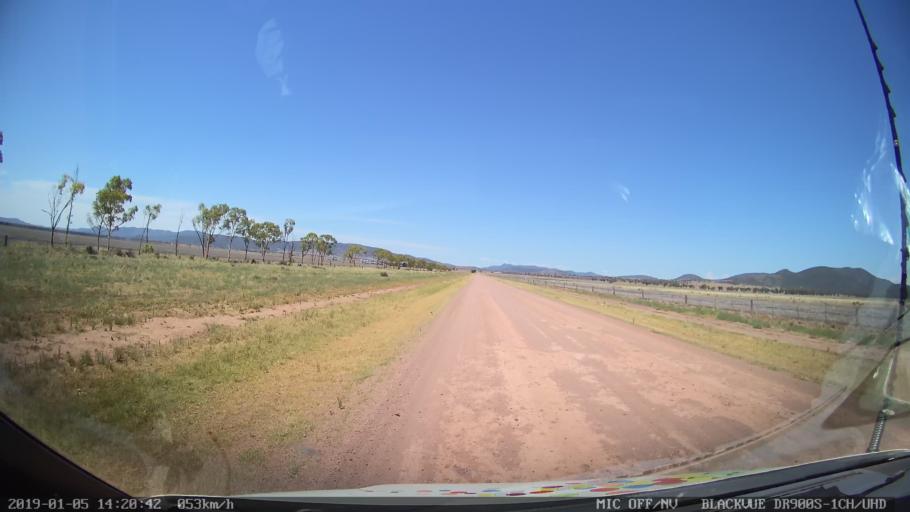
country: AU
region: New South Wales
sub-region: Liverpool Plains
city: Quirindi
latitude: -31.2480
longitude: 150.5071
